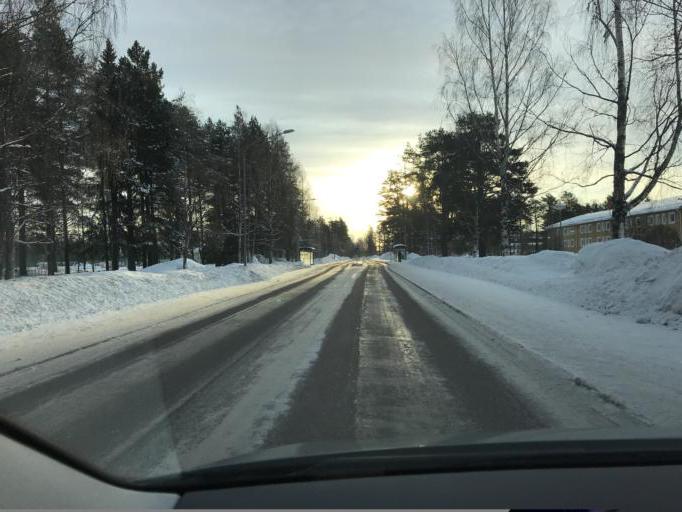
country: SE
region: Norrbotten
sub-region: Lulea Kommun
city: Bergnaset
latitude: 65.6075
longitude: 22.1070
